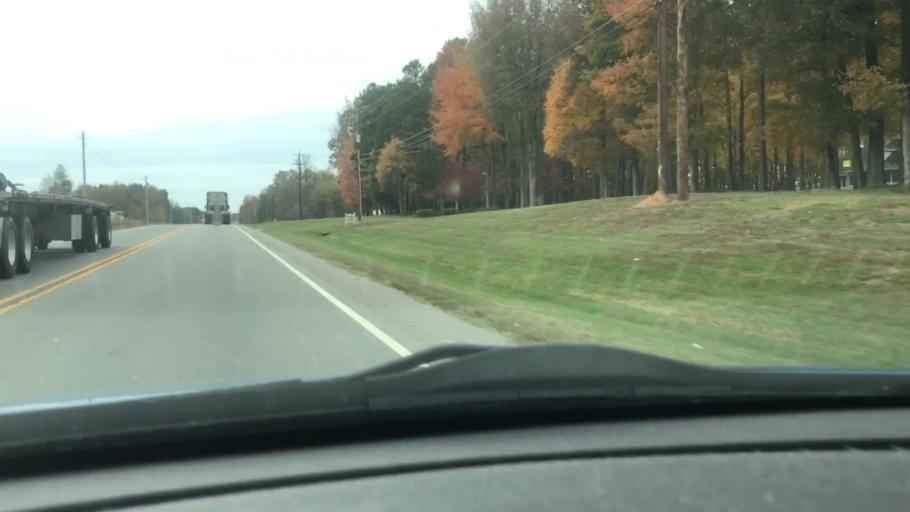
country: US
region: North Carolina
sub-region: Davidson County
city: Thomasville
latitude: 35.7827
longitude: -80.1264
